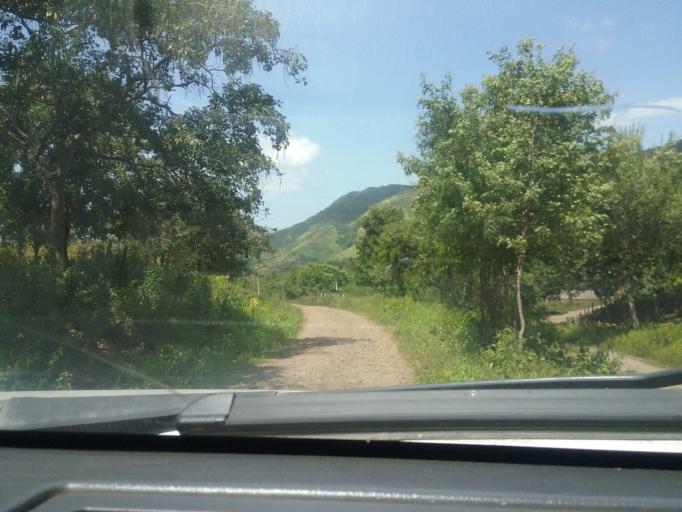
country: NI
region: Matagalpa
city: Terrabona
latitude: 12.6784
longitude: -85.9764
